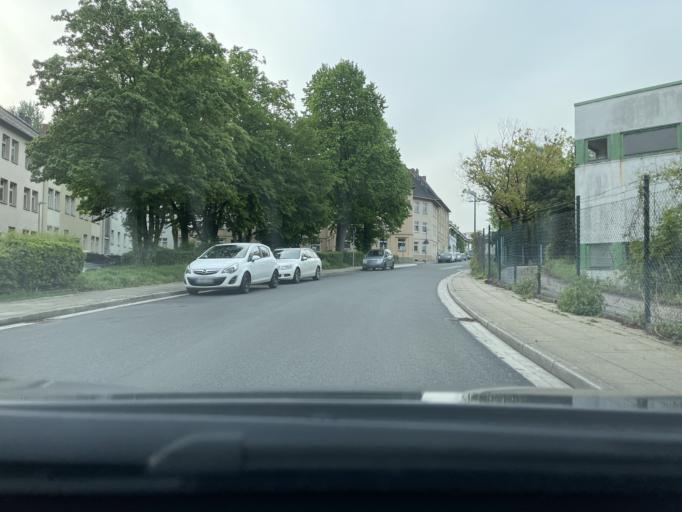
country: DE
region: North Rhine-Westphalia
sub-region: Regierungsbezirk Dusseldorf
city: Essen
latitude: 51.4489
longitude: 6.9885
